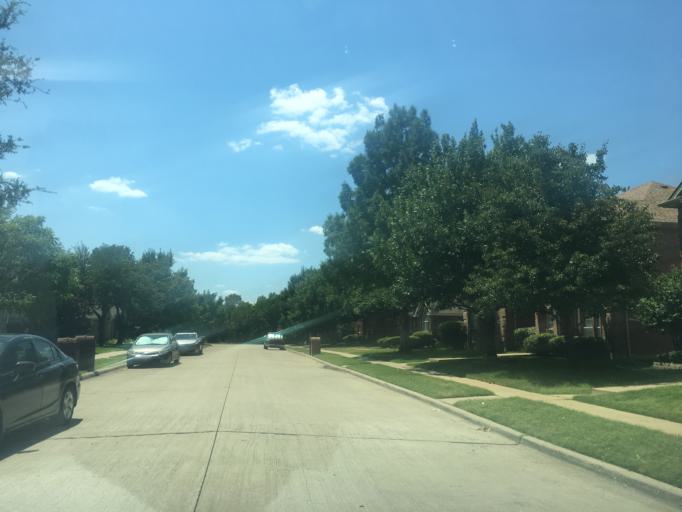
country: US
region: Texas
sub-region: Denton County
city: Lewisville
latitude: 33.0200
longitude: -96.9997
